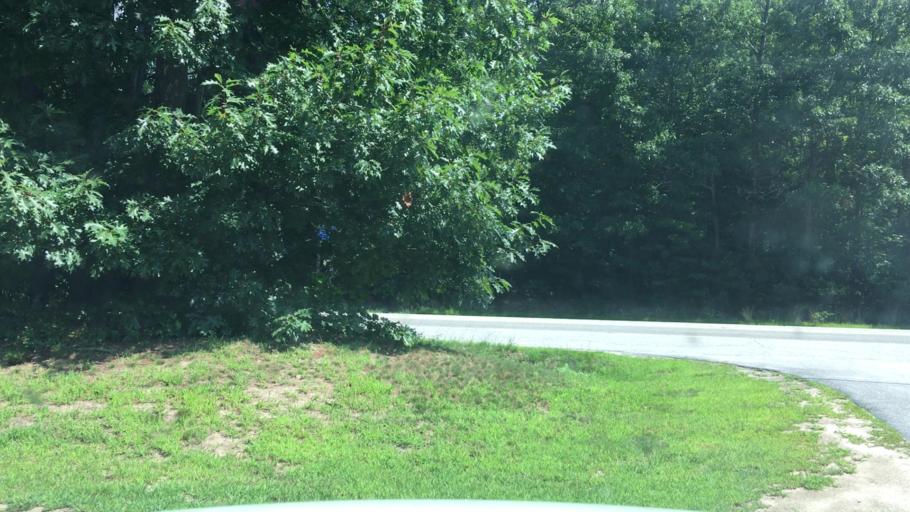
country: US
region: Maine
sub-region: Cumberland County
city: Raymond
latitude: 43.9317
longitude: -70.5392
